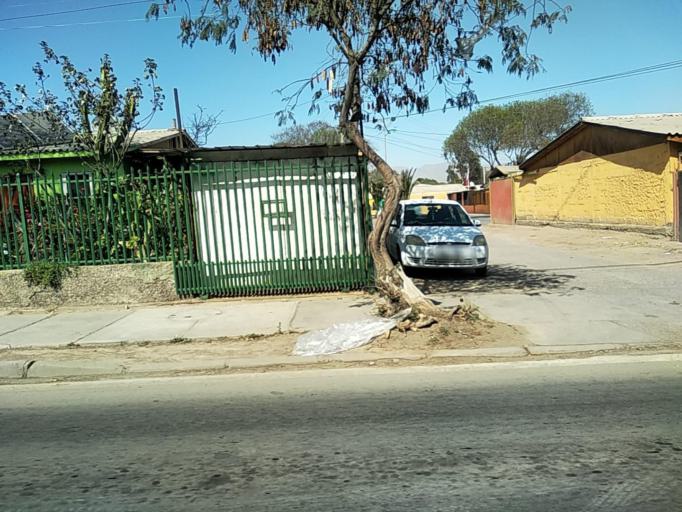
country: CL
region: Atacama
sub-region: Provincia de Copiapo
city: Copiapo
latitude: -27.3781
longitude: -70.3206
